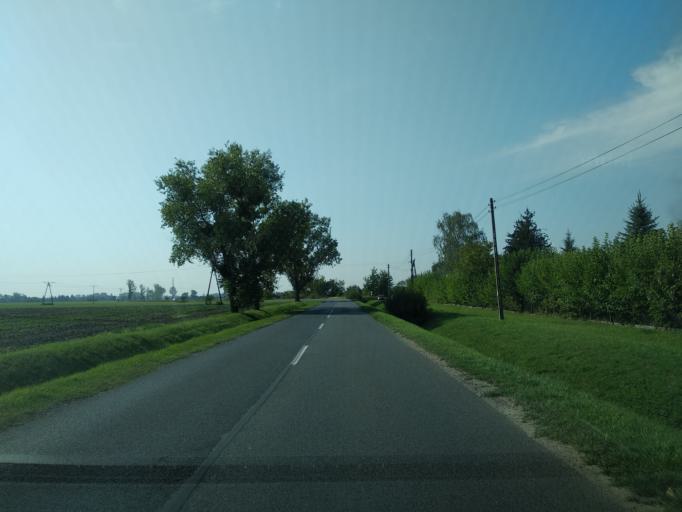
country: PL
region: Lower Silesian Voivodeship
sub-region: Powiat wroclawski
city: Zerniki Wroclawskie
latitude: 51.0452
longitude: 17.0293
